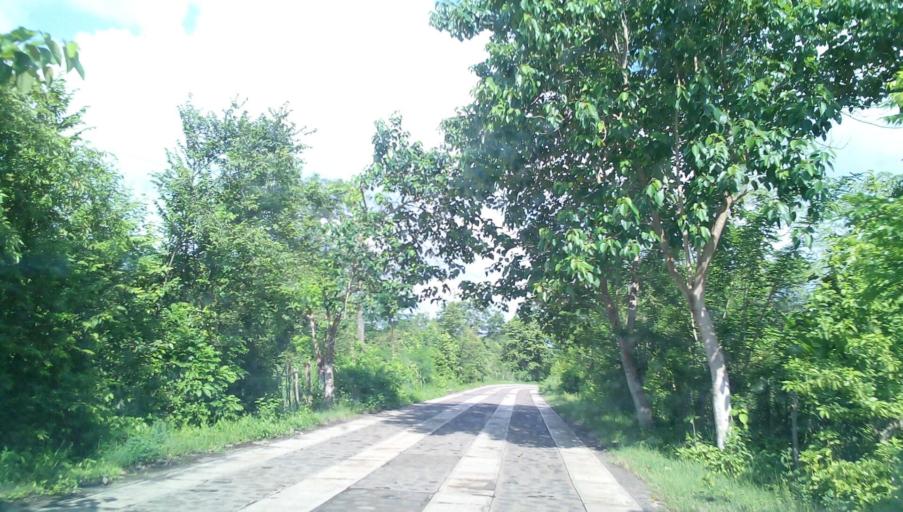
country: MX
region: Veracruz
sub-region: Citlaltepetl
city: Las Sabinas
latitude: 21.3475
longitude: -97.8932
